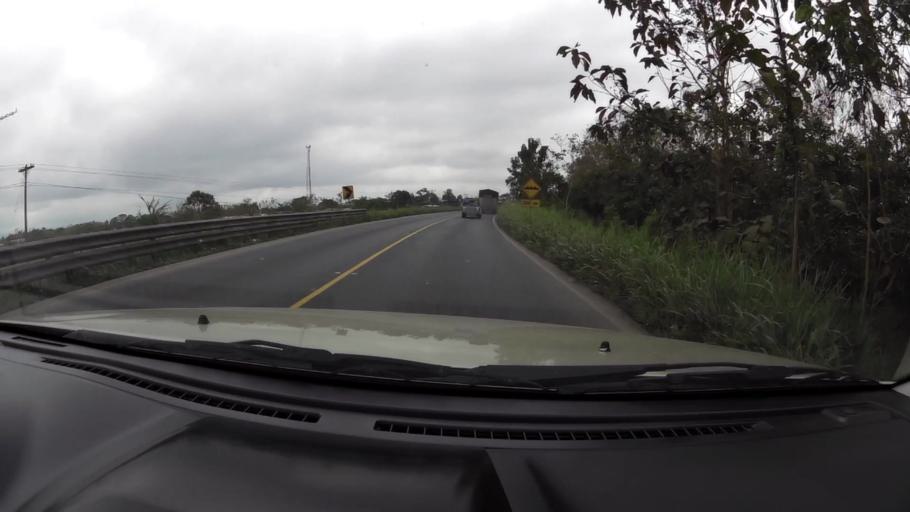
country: EC
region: Guayas
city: Balao
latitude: -2.8201
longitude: -79.7067
